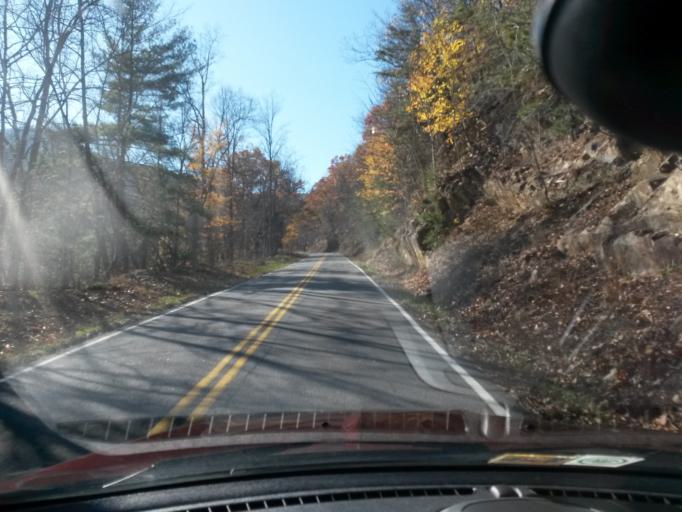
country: US
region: Virginia
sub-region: Botetourt County
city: Buchanan
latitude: 37.5061
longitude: -79.6638
